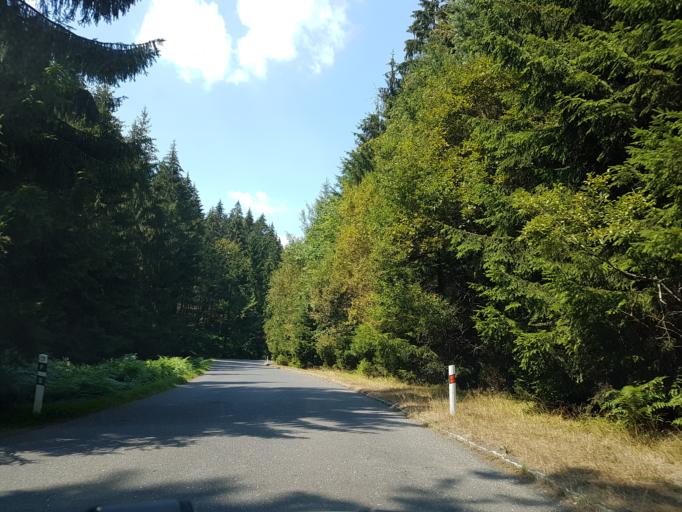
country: DE
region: Saxony
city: Sebnitz
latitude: 50.8789
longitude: 14.2779
